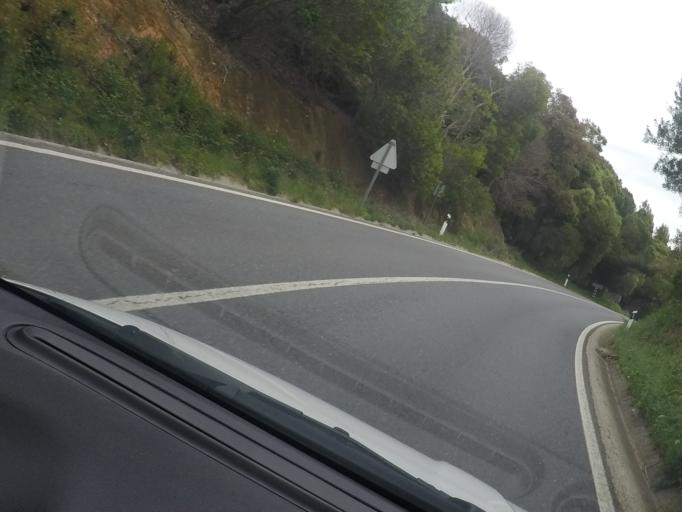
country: PT
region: Setubal
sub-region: Santiago do Cacem
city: Cercal
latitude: 37.7874
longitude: -8.7090
